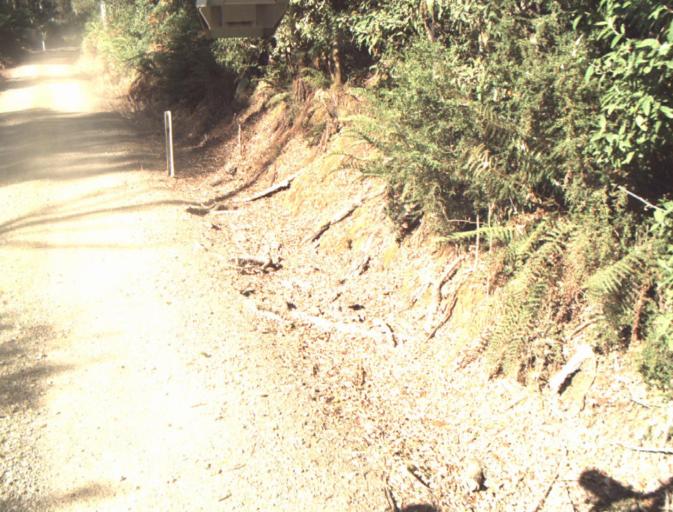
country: AU
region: Tasmania
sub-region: Dorset
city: Scottsdale
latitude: -41.2752
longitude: 147.3626
